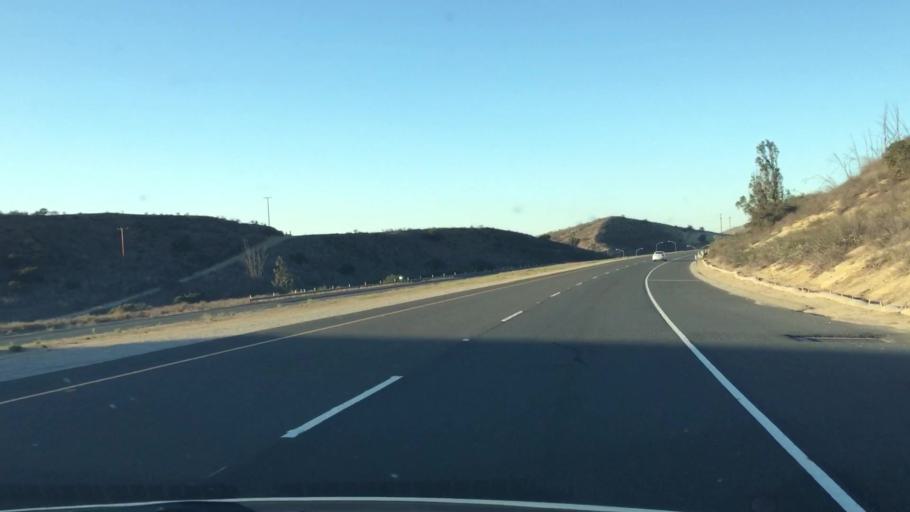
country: US
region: California
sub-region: Orange County
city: Foothill Ranch
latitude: 33.7115
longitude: -117.7198
